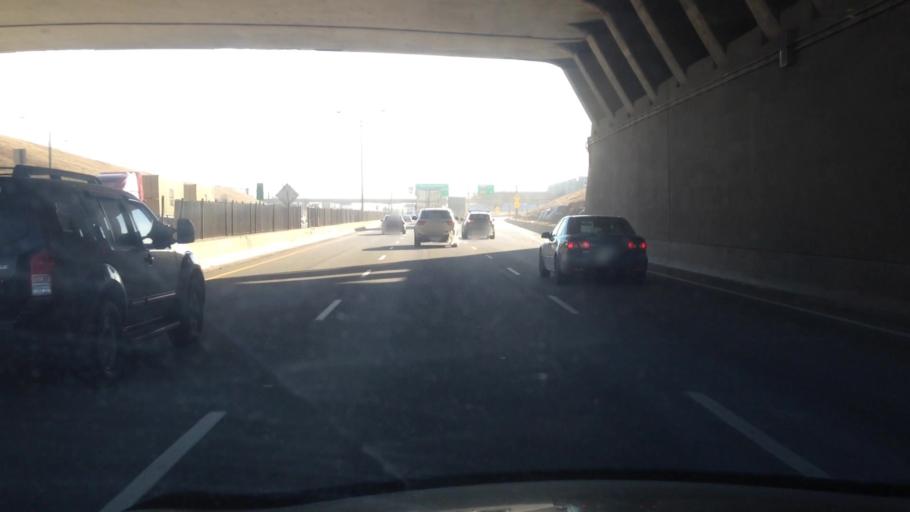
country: CA
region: Quebec
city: Cote-Saint-Luc
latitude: 45.4735
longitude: -73.7082
